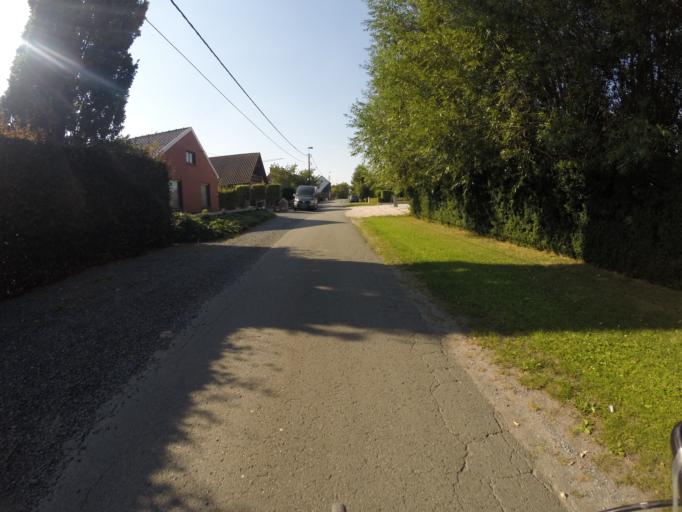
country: BE
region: Flanders
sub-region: Provincie Oost-Vlaanderen
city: Aalter
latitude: 51.0881
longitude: 3.4619
